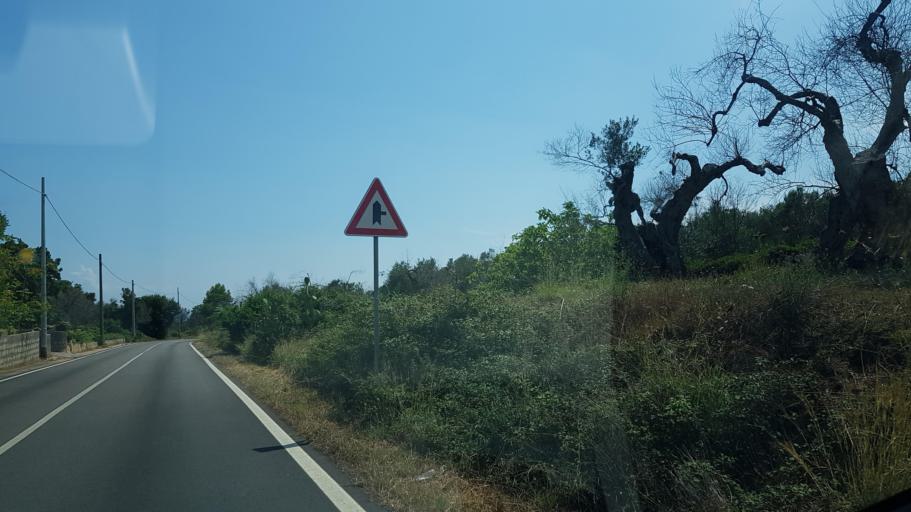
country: IT
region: Apulia
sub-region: Provincia di Lecce
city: Leuca
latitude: 39.8141
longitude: 18.3557
